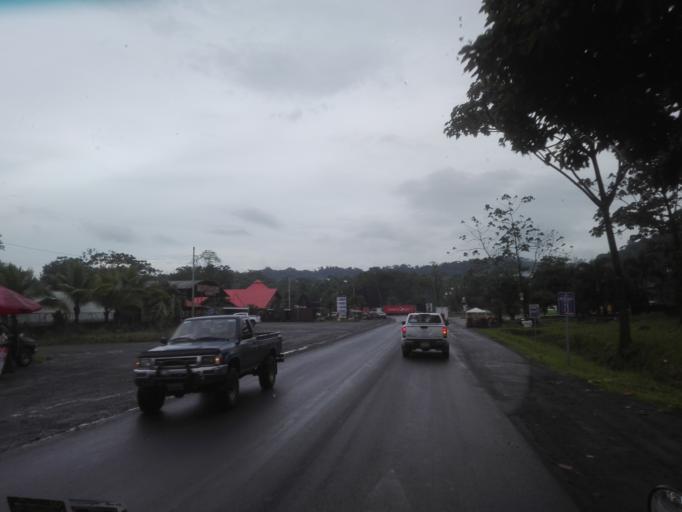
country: CR
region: San Jose
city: Dulce Nombre de Jesus
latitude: 10.2123
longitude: -83.8988
